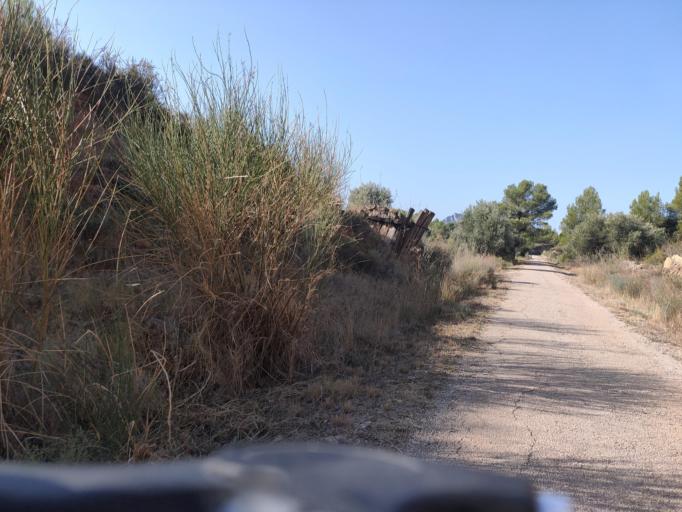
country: ES
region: Catalonia
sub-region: Provincia de Tarragona
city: Bot
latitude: 41.0022
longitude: 0.3741
